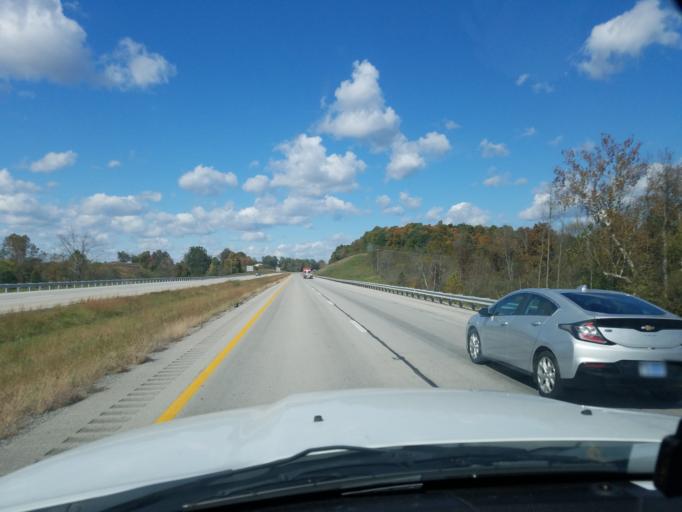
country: US
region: Kentucky
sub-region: Ohio County
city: Hartford
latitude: 37.4773
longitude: -86.9015
